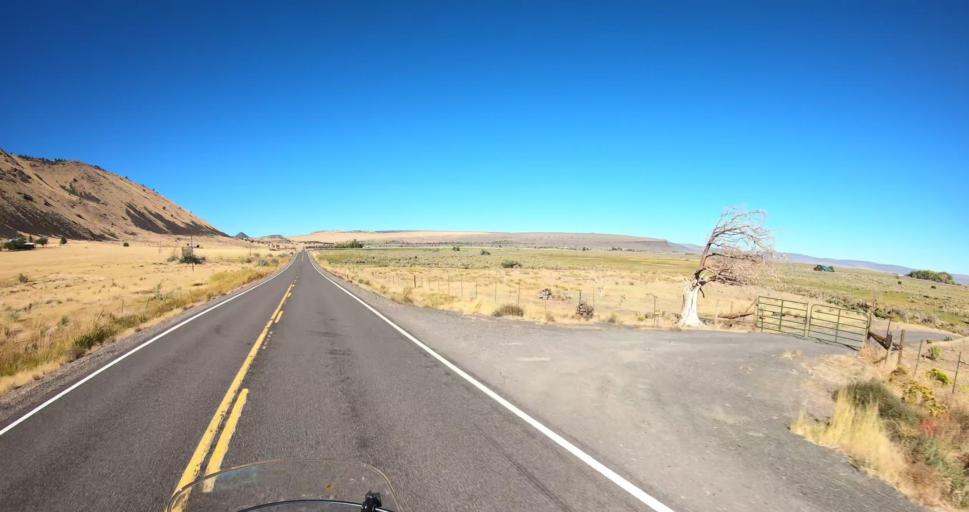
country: US
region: Oregon
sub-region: Lake County
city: Lakeview
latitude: 42.9801
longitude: -120.7774
